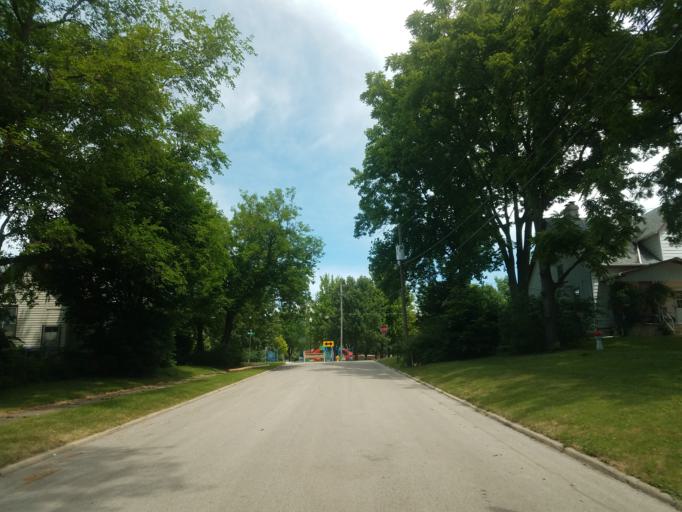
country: US
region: Illinois
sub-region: McLean County
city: Bloomington
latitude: 40.4707
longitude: -88.9837
